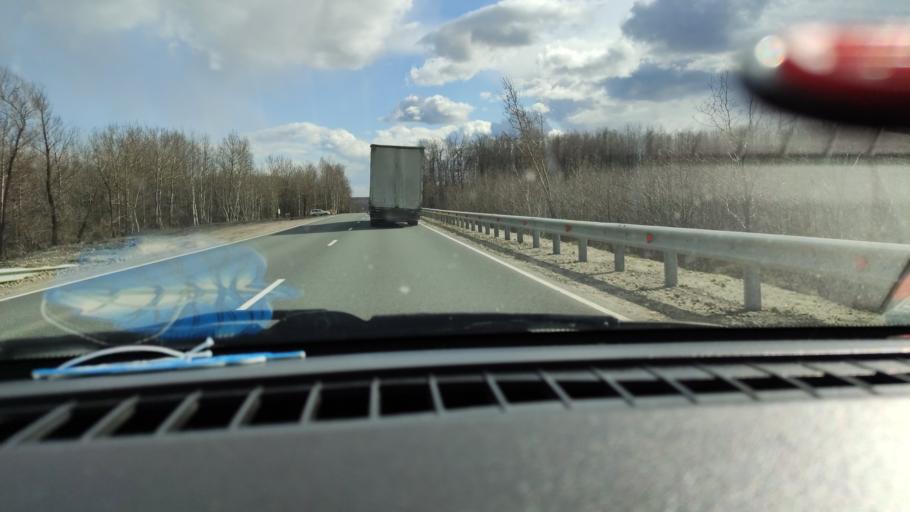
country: RU
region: Saratov
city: Alekseyevka
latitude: 52.4193
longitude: 48.0078
